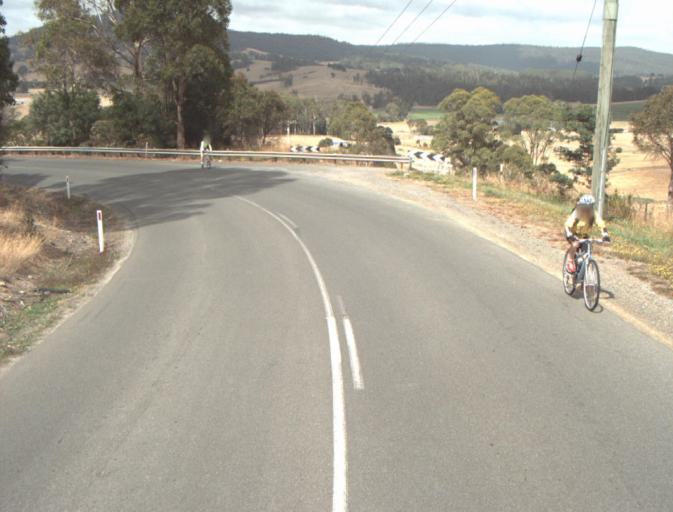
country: AU
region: Tasmania
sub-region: Launceston
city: Mayfield
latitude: -41.2219
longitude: 147.2060
